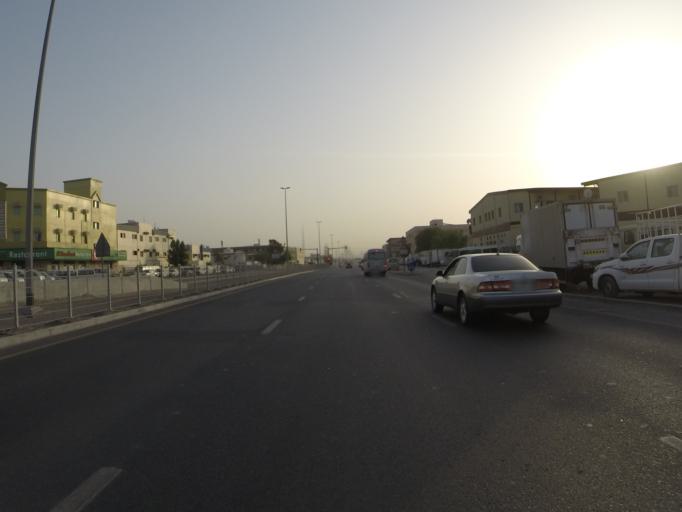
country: AE
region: Dubai
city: Dubai
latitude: 25.1312
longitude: 55.2336
